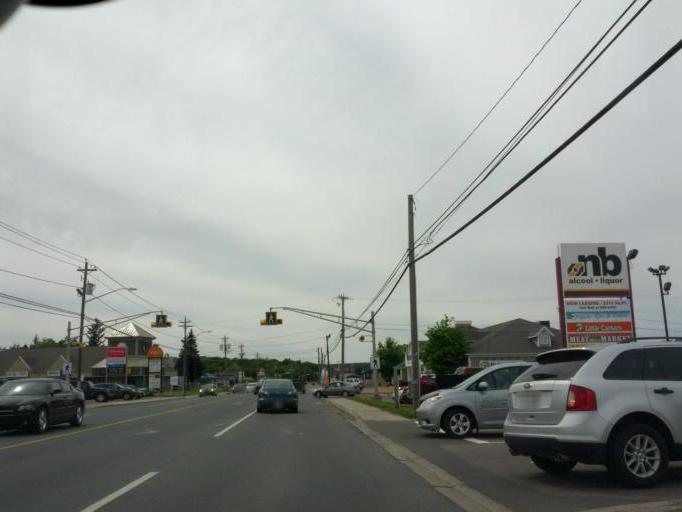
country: CA
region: New Brunswick
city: Moncton
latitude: 46.1220
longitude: -64.8492
